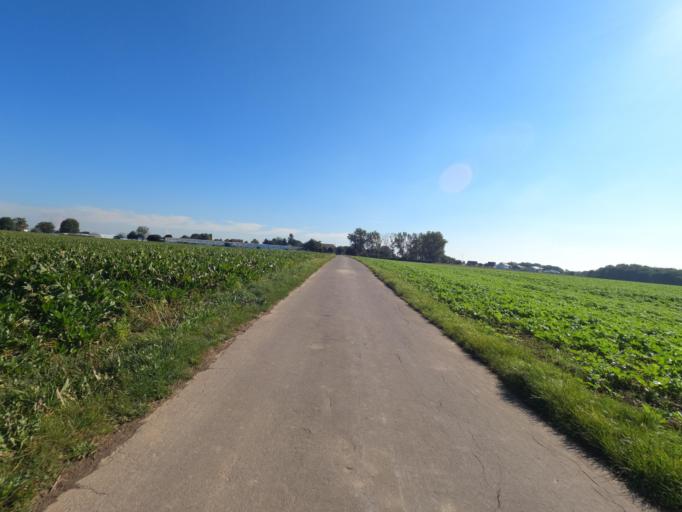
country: DE
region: North Rhine-Westphalia
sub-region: Regierungsbezirk Koln
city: Linnich
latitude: 50.9904
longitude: 6.3006
